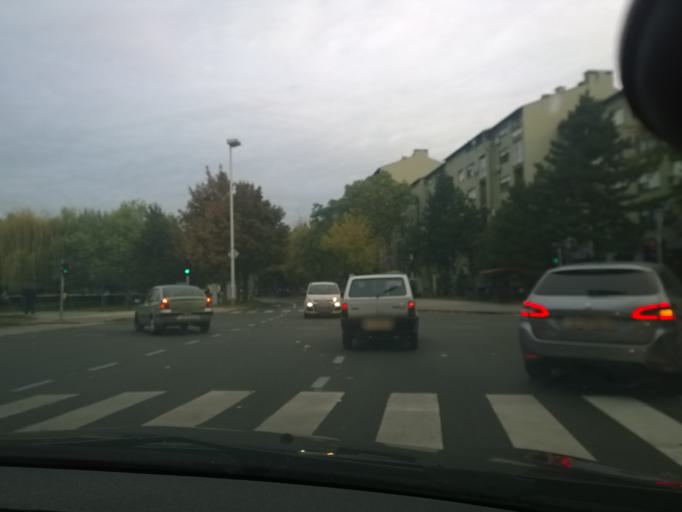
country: HR
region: Grad Zagreb
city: Jankomir
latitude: 45.7894
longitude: 15.9304
